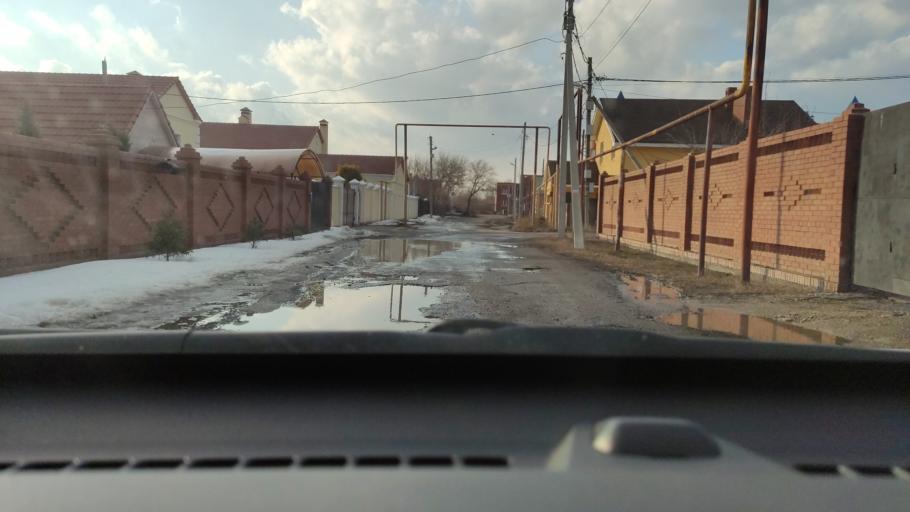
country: RU
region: Samara
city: Podstepki
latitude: 53.5074
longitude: 49.2387
